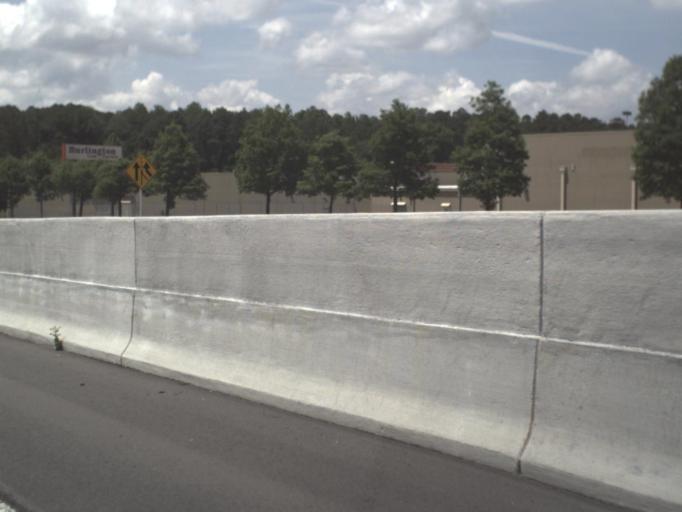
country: US
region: Florida
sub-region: Clay County
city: Bellair-Meadowbrook Terrace
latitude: 30.1977
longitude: -81.7418
